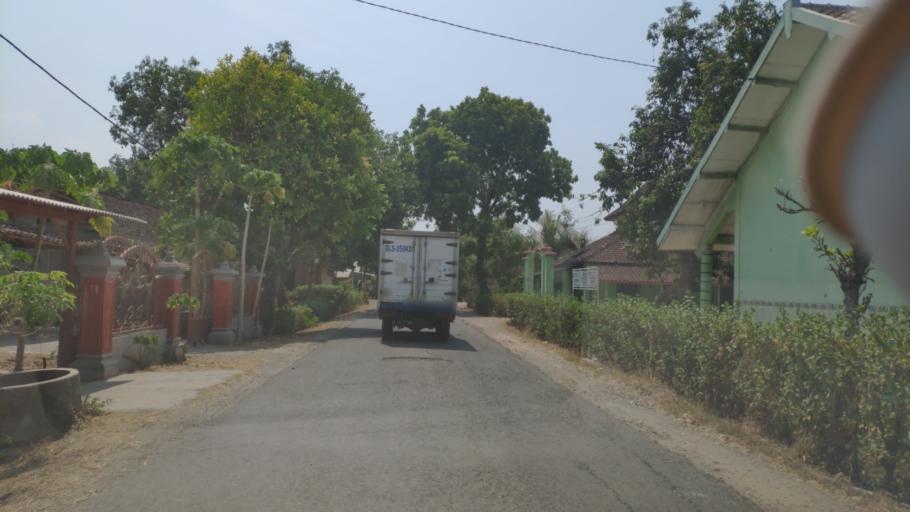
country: ID
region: Central Java
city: Kadengan
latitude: -7.1761
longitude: 111.3856
